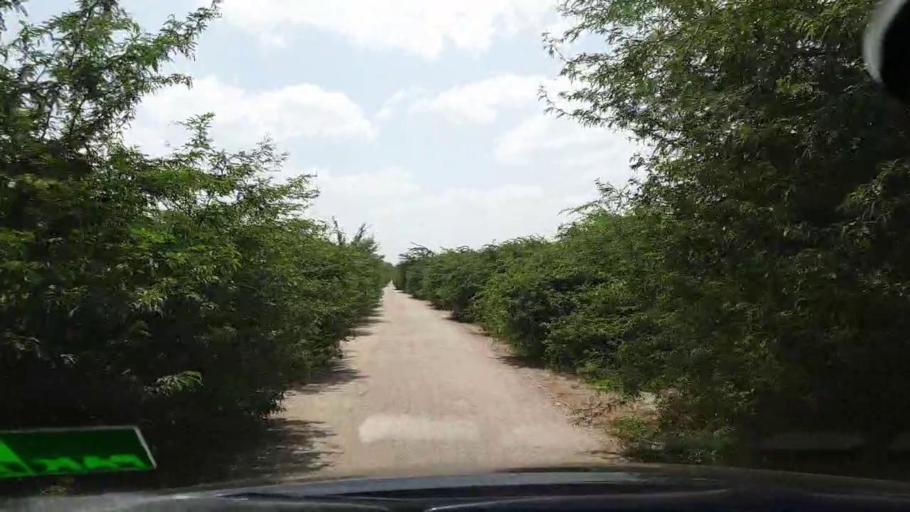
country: PK
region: Sindh
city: Kadhan
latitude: 24.5694
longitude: 69.2111
